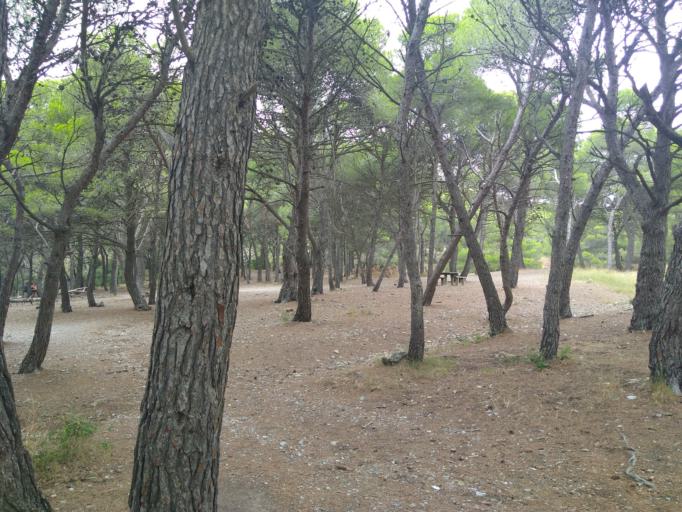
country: FR
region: Languedoc-Roussillon
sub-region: Departement de l'Aude
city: Gruissan
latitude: 43.1305
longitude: 3.0999
